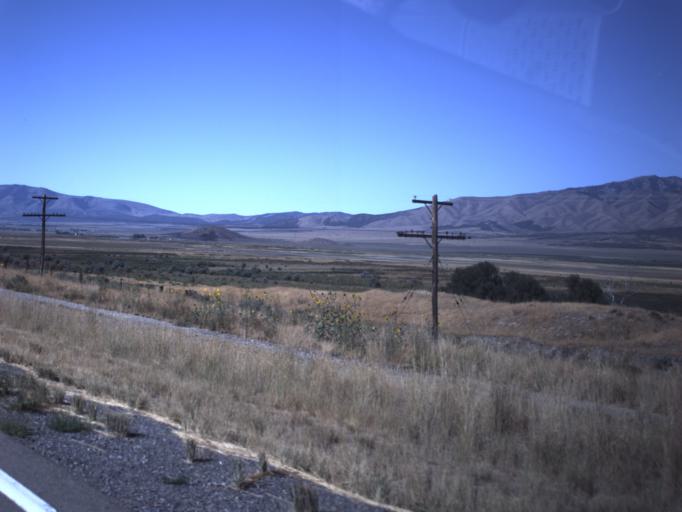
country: US
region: Utah
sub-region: Tooele County
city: Tooele
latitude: 40.4290
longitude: -112.3795
